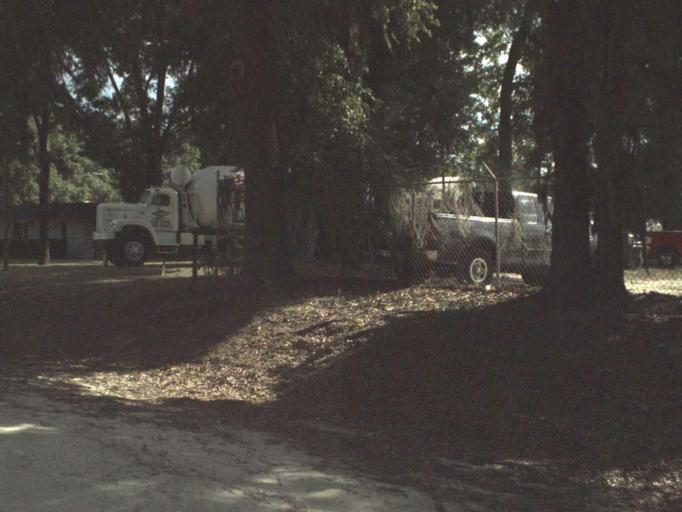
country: US
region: Florida
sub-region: Marion County
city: Belleview
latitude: 29.0696
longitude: -82.0536
